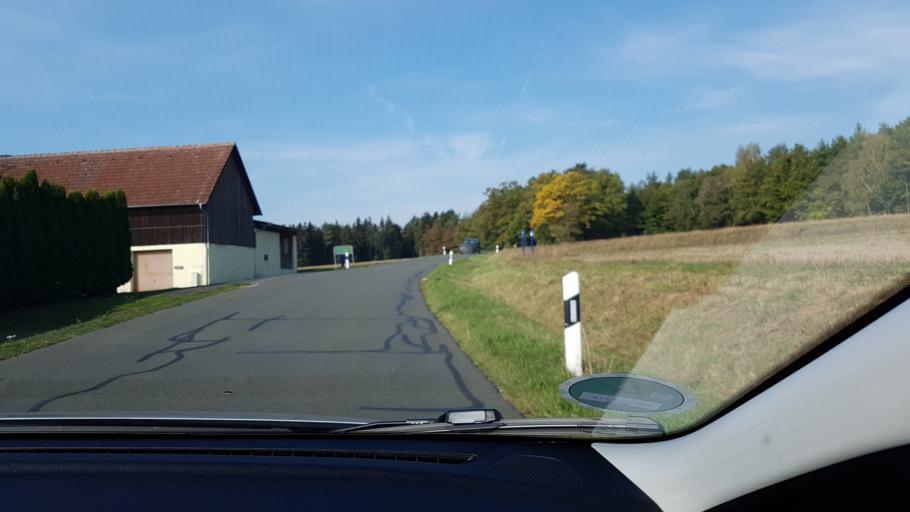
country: DE
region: Bavaria
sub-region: Upper Franconia
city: Waischenfeld
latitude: 49.8230
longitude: 11.3609
